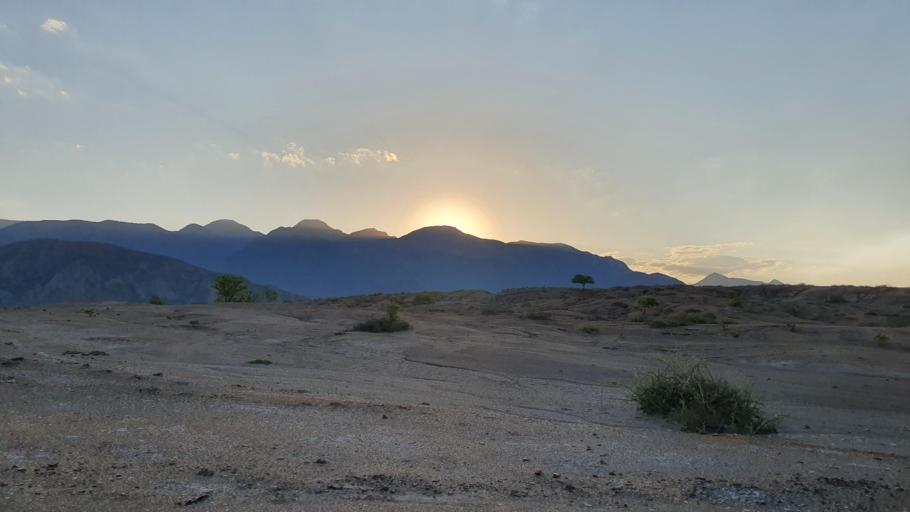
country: BO
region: Chuquisaca
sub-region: Provincia Zudanez
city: Mojocoya
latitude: -18.6868
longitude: -64.5154
